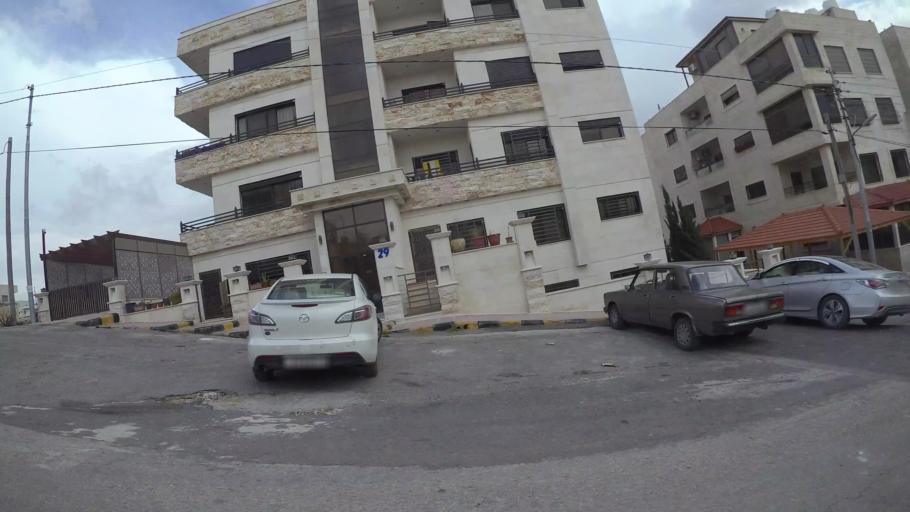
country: JO
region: Amman
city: Umm as Summaq
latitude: 31.8828
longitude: 35.8654
